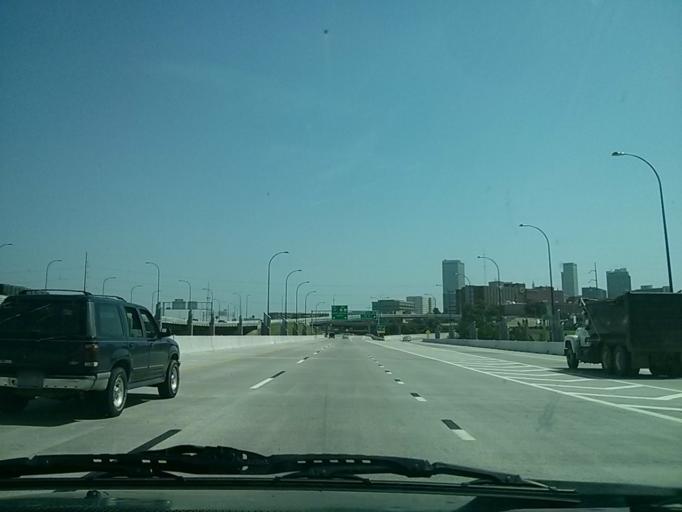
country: US
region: Oklahoma
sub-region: Tulsa County
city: Tulsa
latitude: 36.1432
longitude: -96.0051
